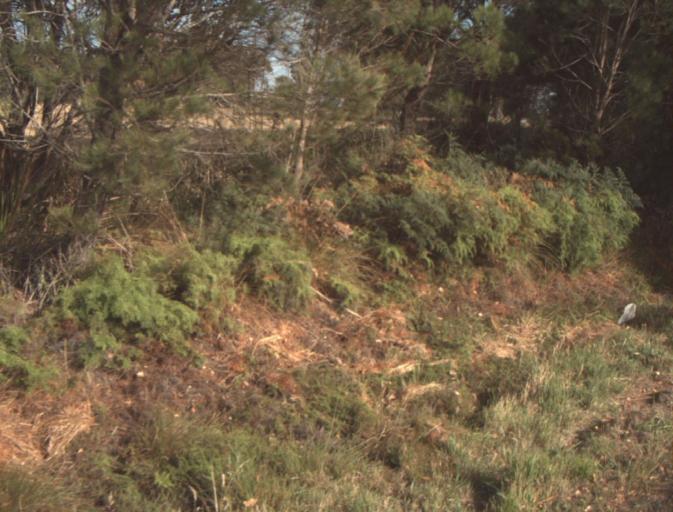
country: AU
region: Tasmania
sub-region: Dorset
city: Bridport
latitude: -41.1106
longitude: 147.2006
